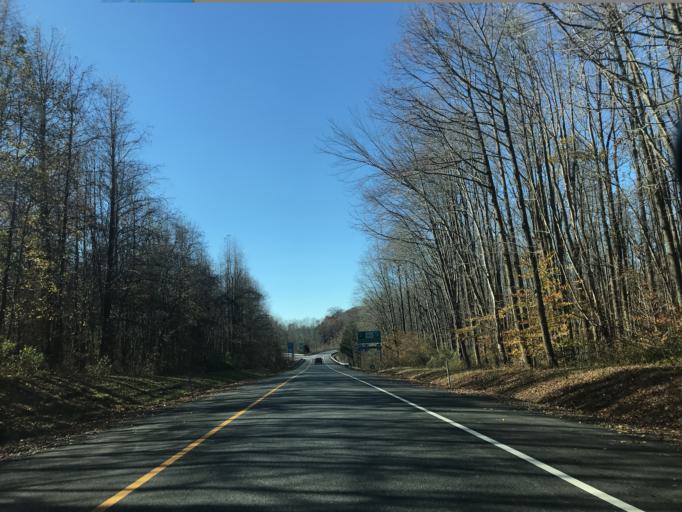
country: US
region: Maryland
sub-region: Harford County
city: Havre de Grace
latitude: 39.5739
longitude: -76.1368
